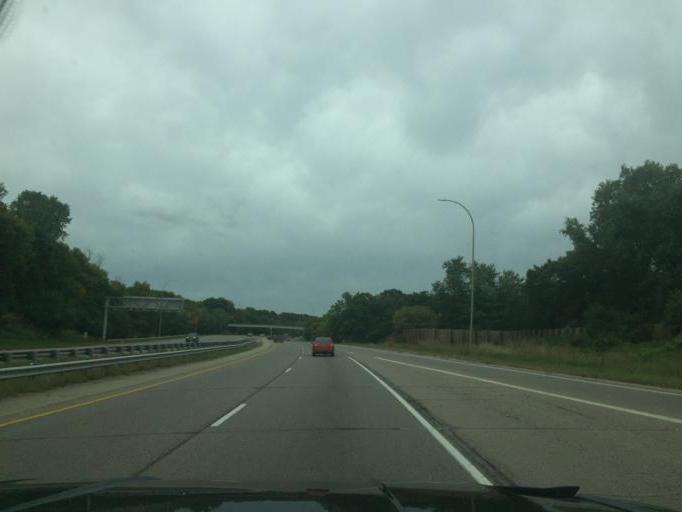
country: US
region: Minnesota
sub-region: Dakota County
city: South Saint Paul
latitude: 44.9038
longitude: -93.0652
